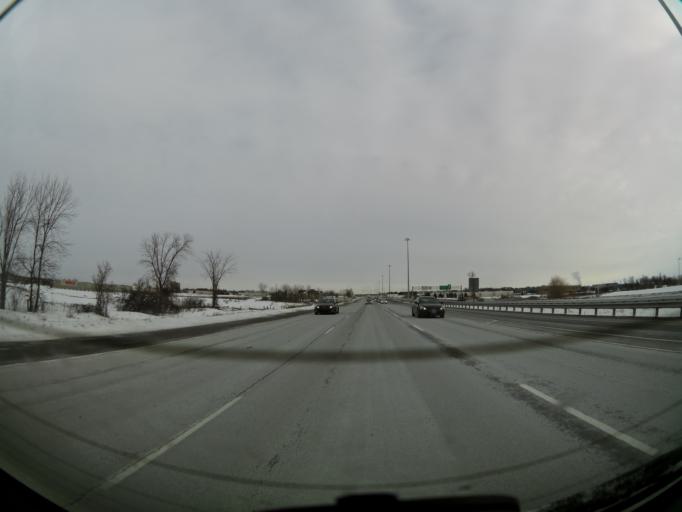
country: CA
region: Ontario
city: Bells Corners
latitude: 45.3011
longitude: -75.9240
